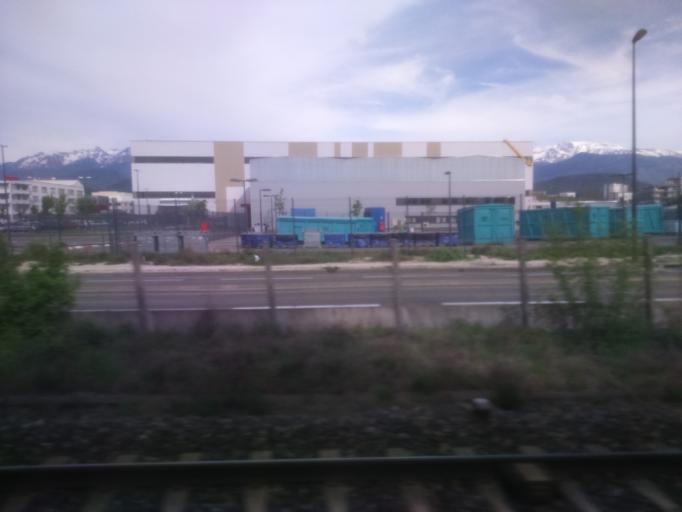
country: FR
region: Rhone-Alpes
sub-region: Departement de l'Isere
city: Grenoble
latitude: 45.1636
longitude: 5.7127
